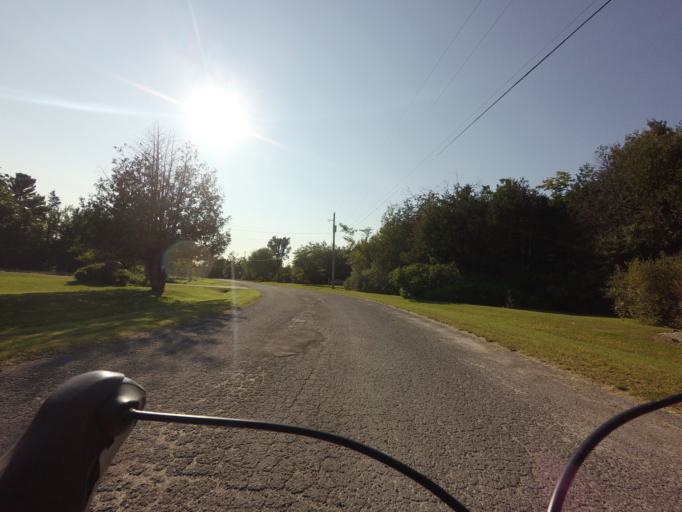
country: CA
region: Ontario
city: Bells Corners
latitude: 45.4802
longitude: -76.0361
